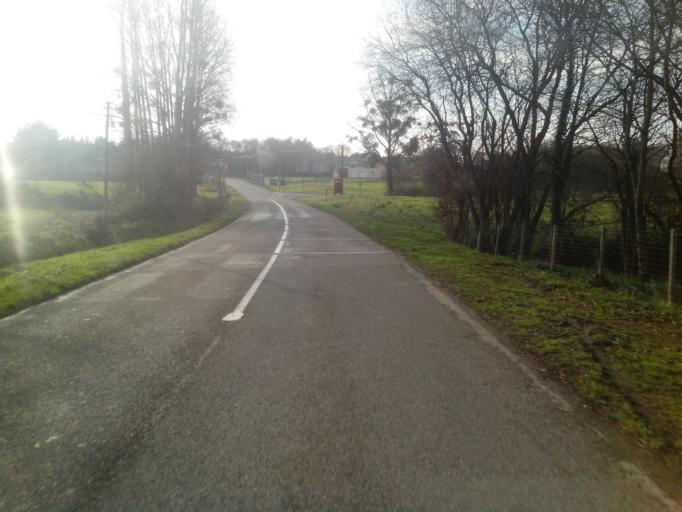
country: FR
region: Brittany
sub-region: Departement du Morbihan
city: Mauron
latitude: 48.0881
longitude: -2.2801
